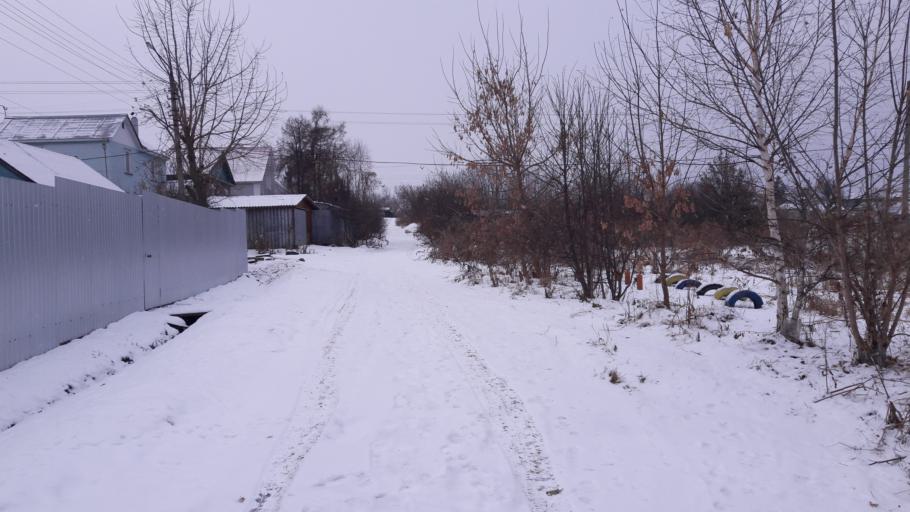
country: RU
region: Tula
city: Gorelki
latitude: 54.2363
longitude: 37.6354
